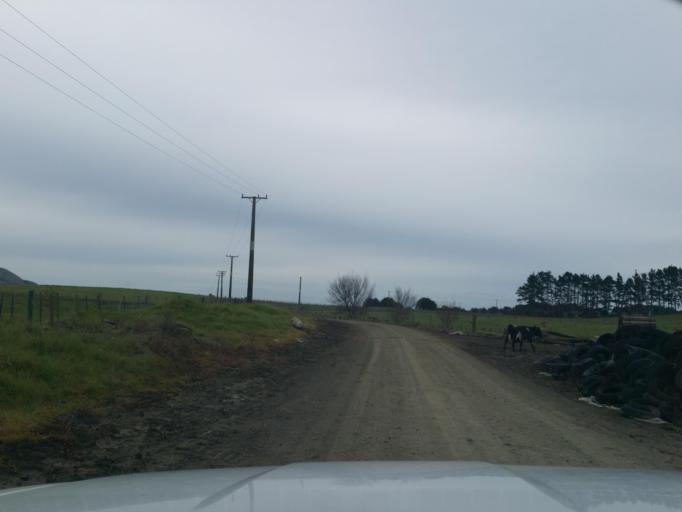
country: NZ
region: Northland
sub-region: Whangarei
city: Maungatapere
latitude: -35.8021
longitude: 174.0500
